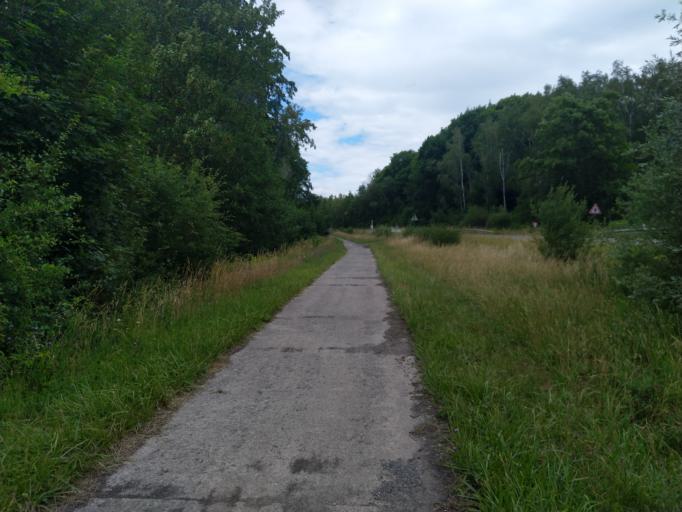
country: BE
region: Wallonia
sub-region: Province du Hainaut
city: Bernissart
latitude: 50.4952
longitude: 3.6424
